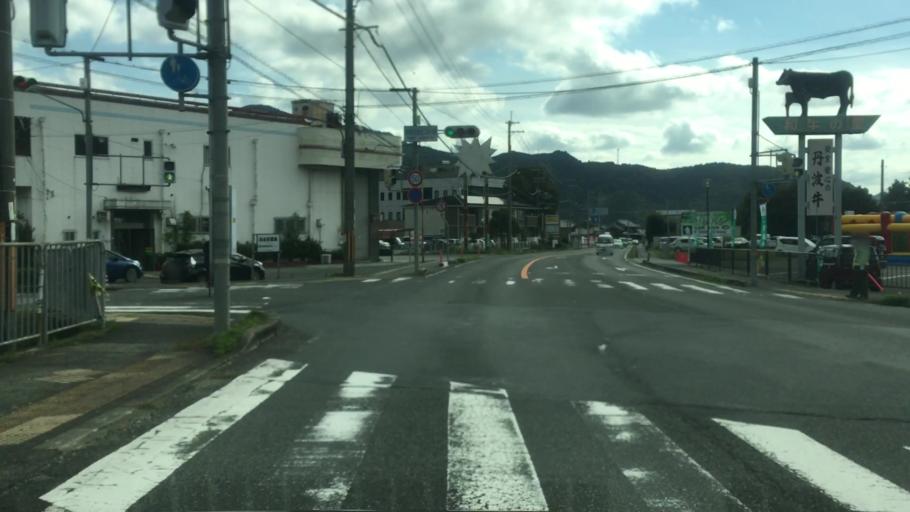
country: JP
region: Kyoto
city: Fukuchiyama
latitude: 35.2497
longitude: 135.0027
